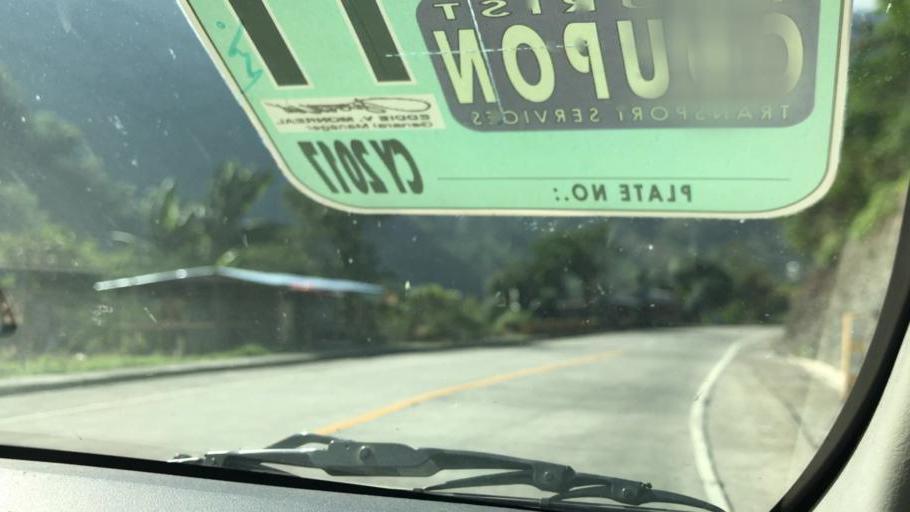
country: PH
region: Cordillera
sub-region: Province of Benguet
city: Tuba
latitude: 16.3175
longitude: 120.6175
